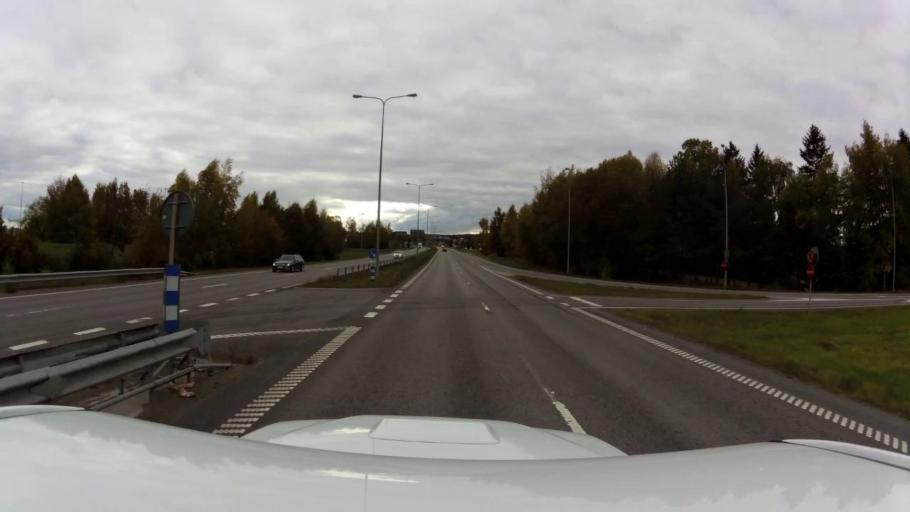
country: SE
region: OEstergoetland
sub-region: Linkopings Kommun
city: Linkoping
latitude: 58.4369
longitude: 15.5822
